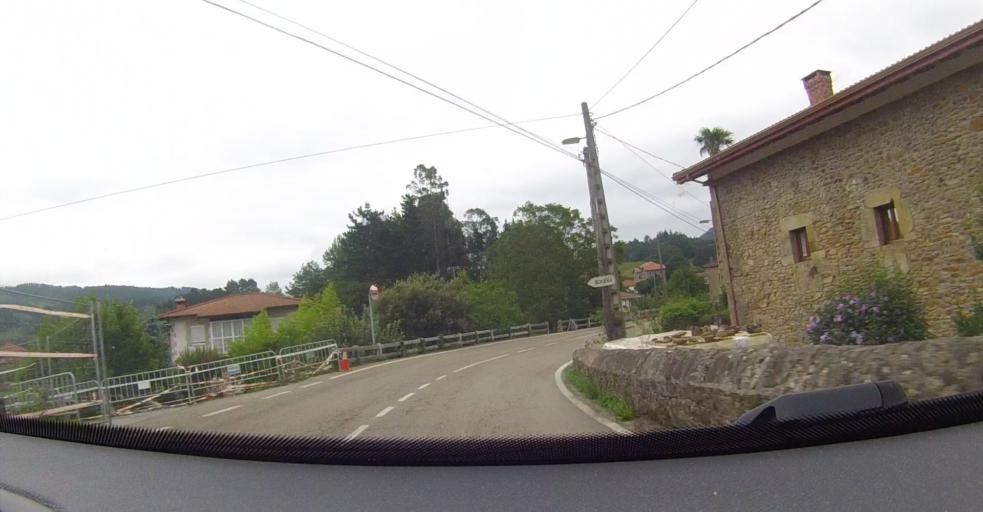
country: ES
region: Basque Country
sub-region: Bizkaia
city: Balmaseda
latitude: 43.2447
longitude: -3.2654
